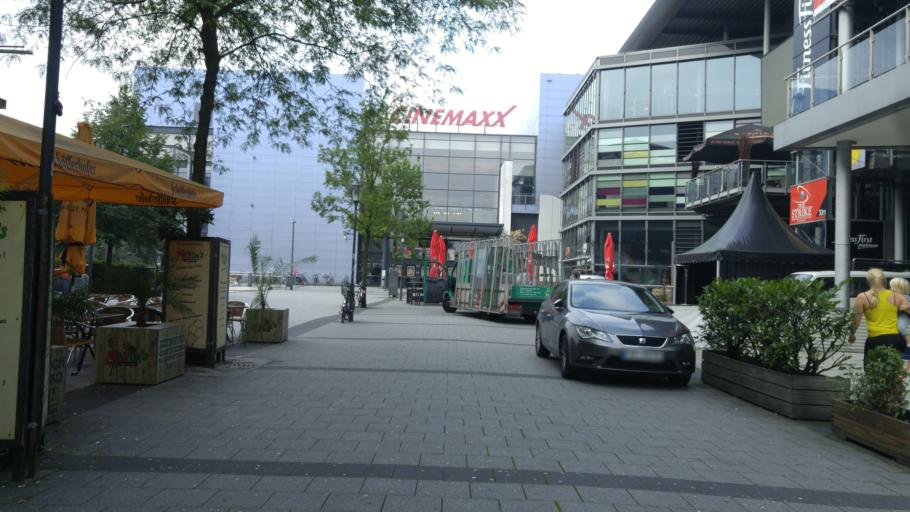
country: DE
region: North Rhine-Westphalia
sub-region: Regierungsbezirk Detmold
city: Bielefeld
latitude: 52.0303
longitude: 8.5319
